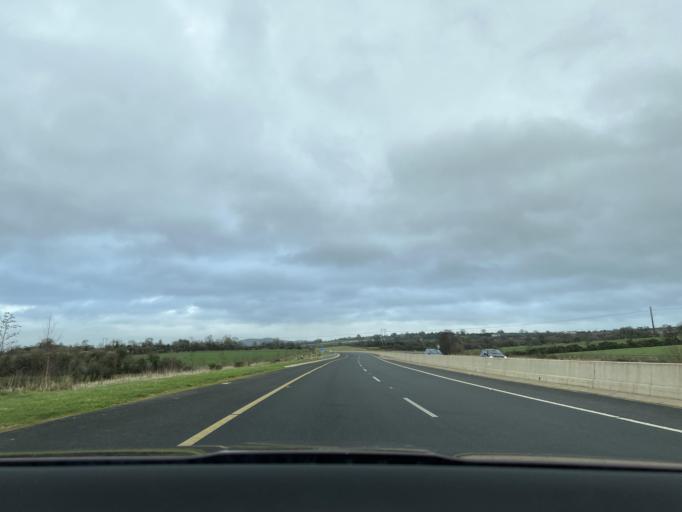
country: IE
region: Leinster
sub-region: Loch Garman
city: Ferns
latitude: 52.5624
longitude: -6.4630
